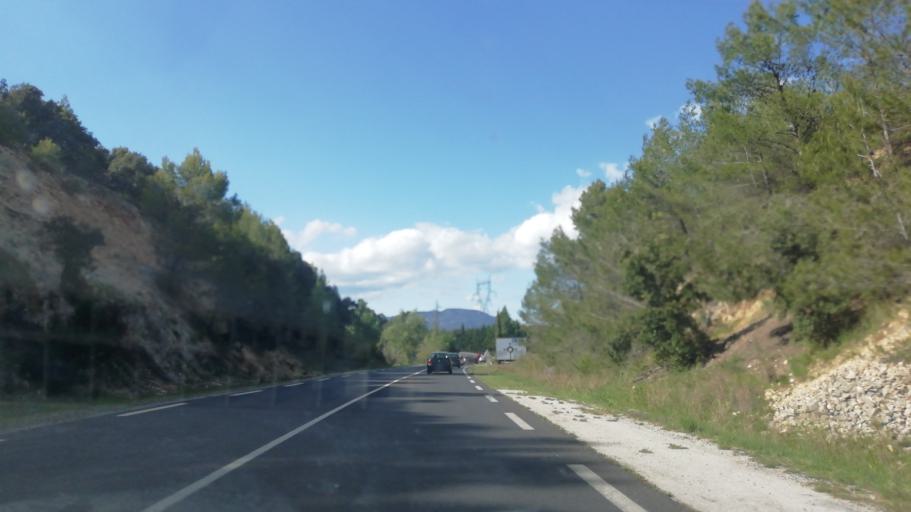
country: FR
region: Languedoc-Roussillon
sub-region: Departement de l'Herault
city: Saint-Gely-du-Fesc
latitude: 43.7054
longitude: 3.8189
